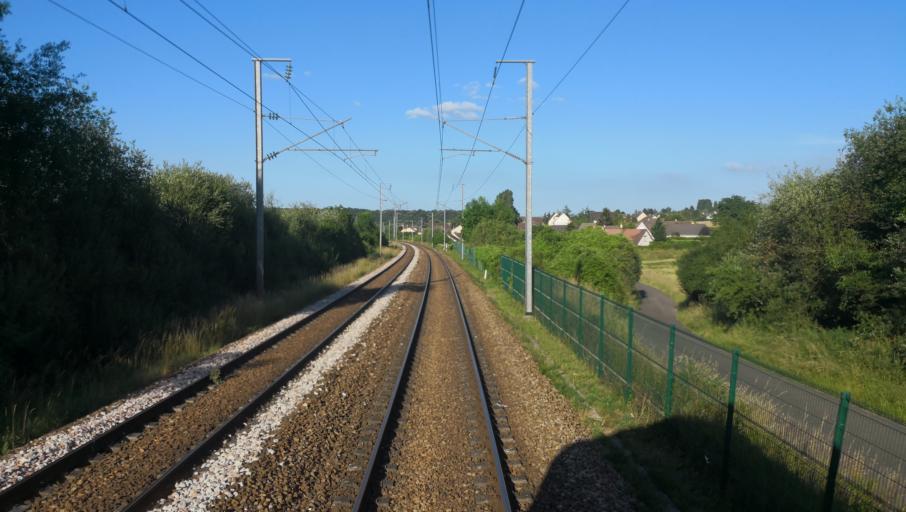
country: FR
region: Haute-Normandie
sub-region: Departement de l'Eure
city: Arnieres-sur-Iton
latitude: 48.9944
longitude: 1.0902
